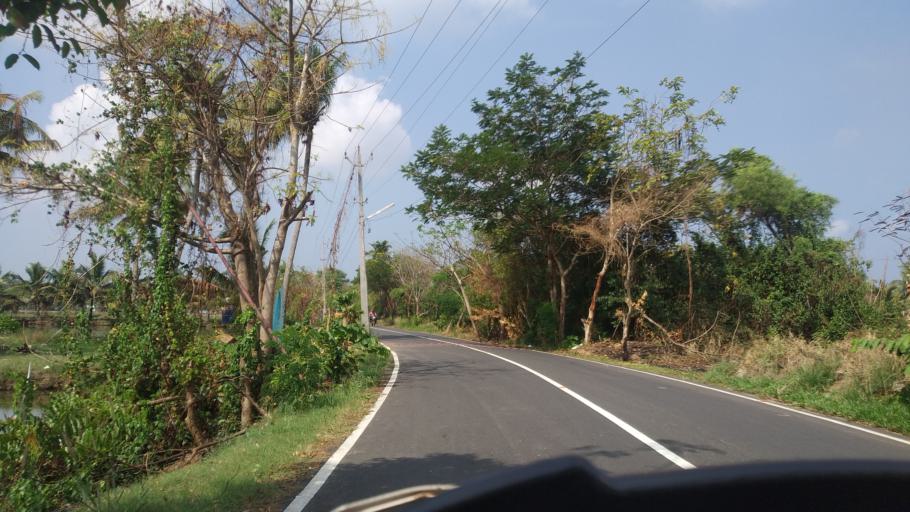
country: IN
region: Kerala
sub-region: Ernakulam
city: Elur
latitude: 10.1140
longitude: 76.2341
